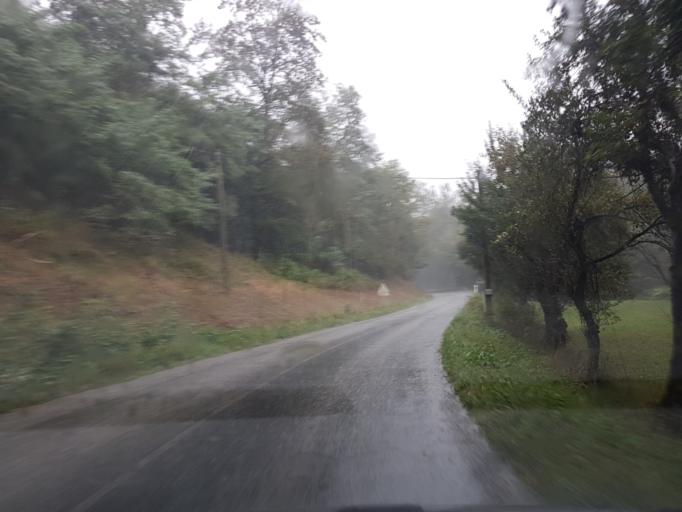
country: FR
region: Midi-Pyrenees
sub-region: Departement de l'Ariege
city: Saint-Girons
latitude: 42.9002
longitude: 1.3055
